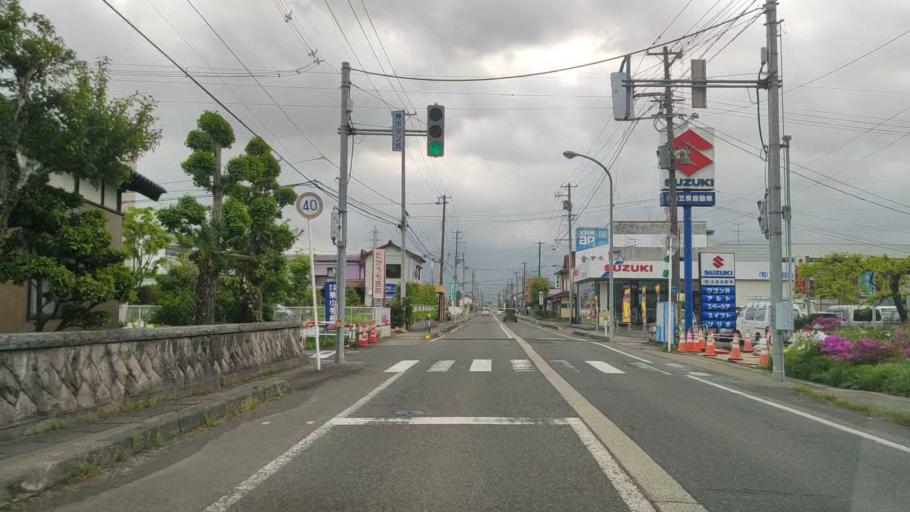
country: JP
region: Niigata
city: Gosen
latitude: 37.7350
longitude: 139.1933
